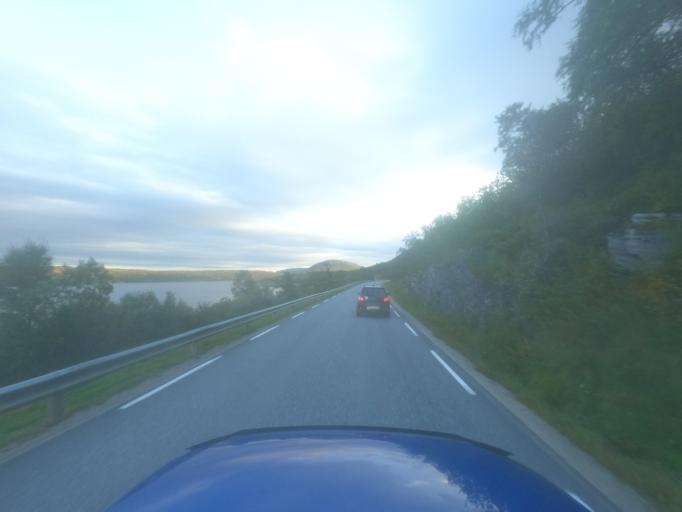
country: NO
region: Finnmark Fylke
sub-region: Porsanger
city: Lakselv
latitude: 70.3404
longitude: 25.0767
